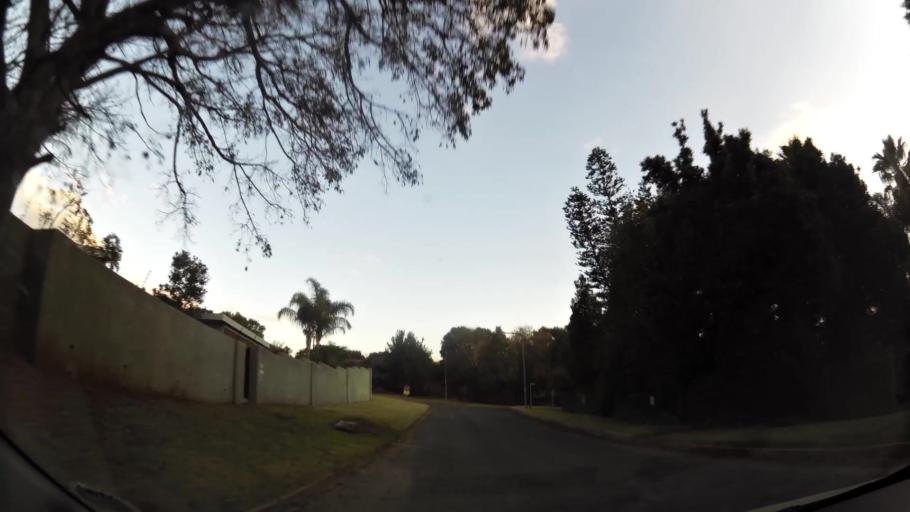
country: ZA
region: Gauteng
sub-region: West Rand District Municipality
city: Krugersdorp
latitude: -26.0741
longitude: 27.7805
